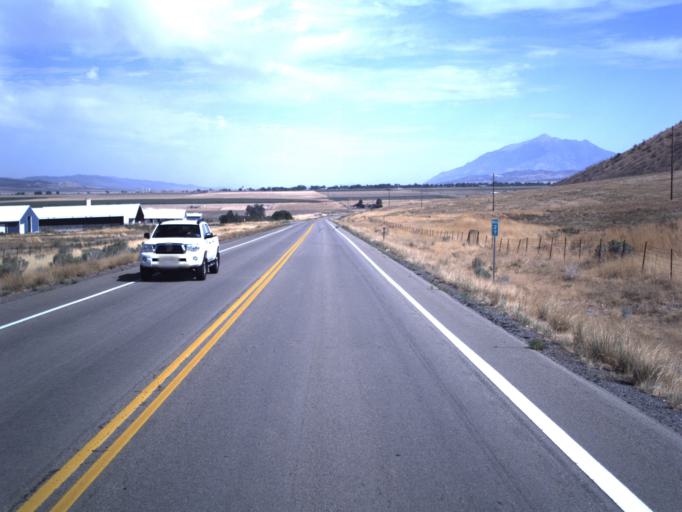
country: US
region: Utah
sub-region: Juab County
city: Nephi
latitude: 39.5158
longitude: -111.8680
